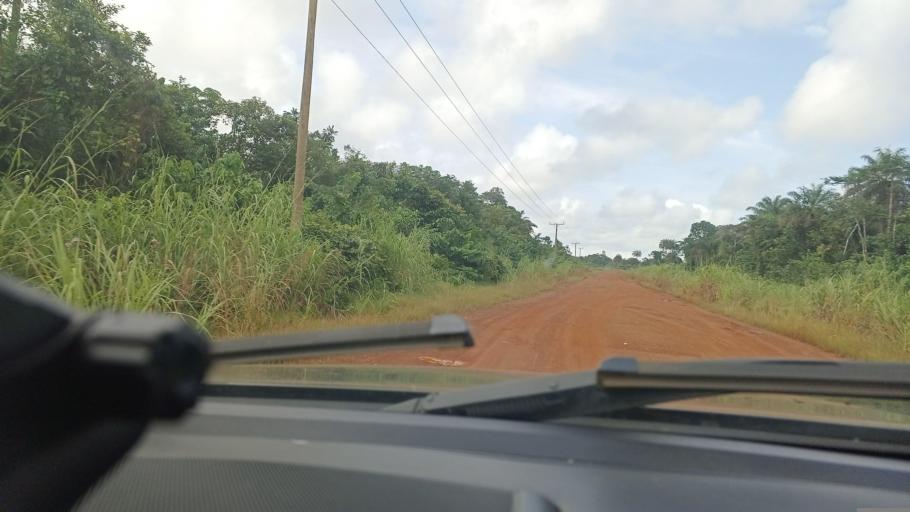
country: LR
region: Grand Cape Mount
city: Robertsport
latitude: 6.6815
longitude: -11.1322
